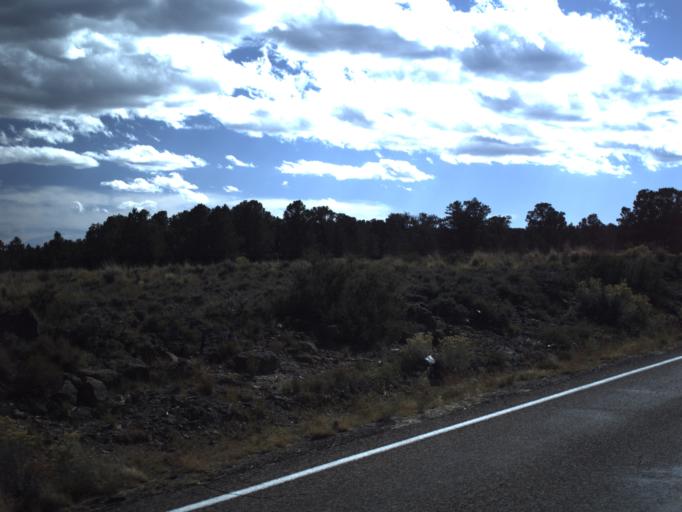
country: US
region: Utah
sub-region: Garfield County
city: Panguitch
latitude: 37.7715
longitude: -112.4466
